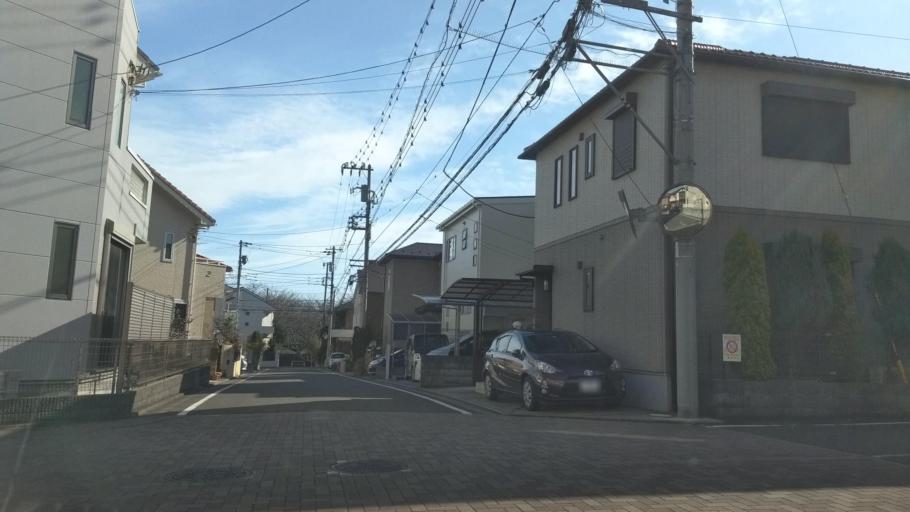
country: JP
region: Kanagawa
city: Hadano
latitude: 35.3562
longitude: 139.2265
